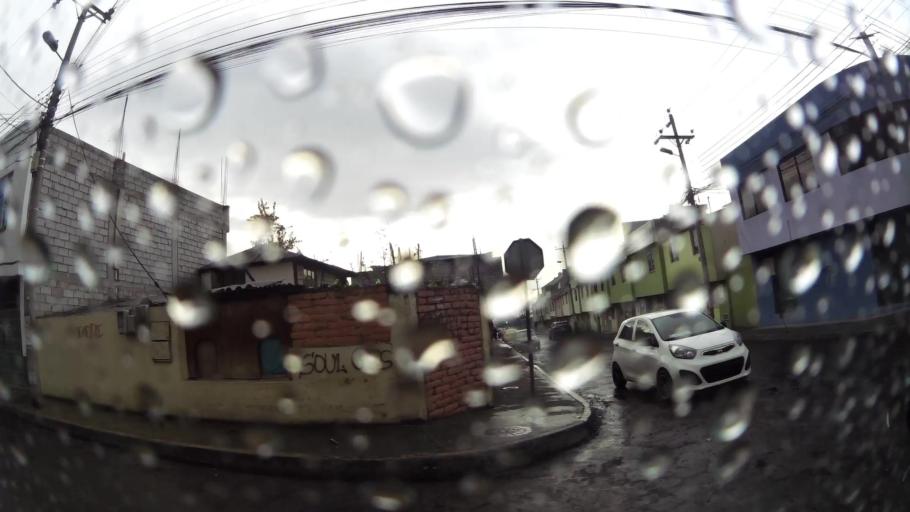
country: EC
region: Pichincha
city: Quito
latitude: -0.3054
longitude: -78.5482
